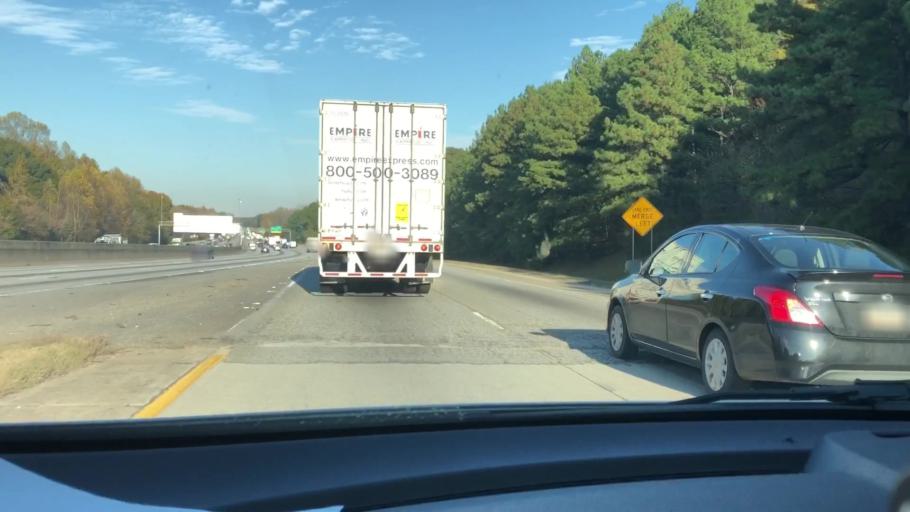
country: US
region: Georgia
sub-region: DeKalb County
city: Gresham Park
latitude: 33.6761
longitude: -84.3205
